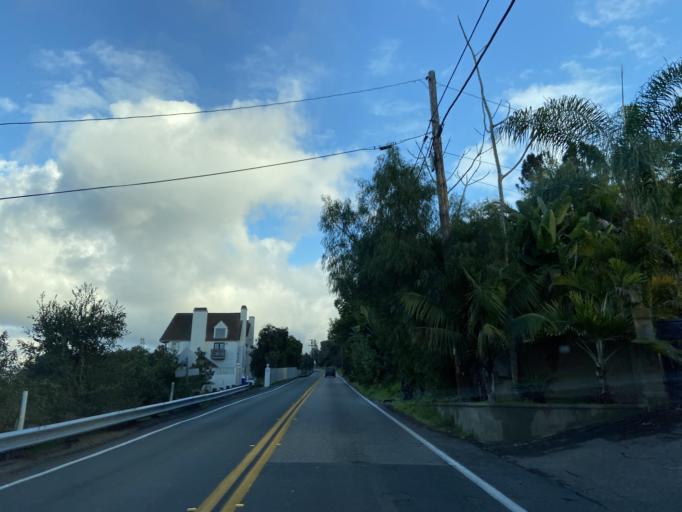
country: US
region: California
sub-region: San Diego County
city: Casa de Oro-Mount Helix
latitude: 32.7770
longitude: -116.9916
